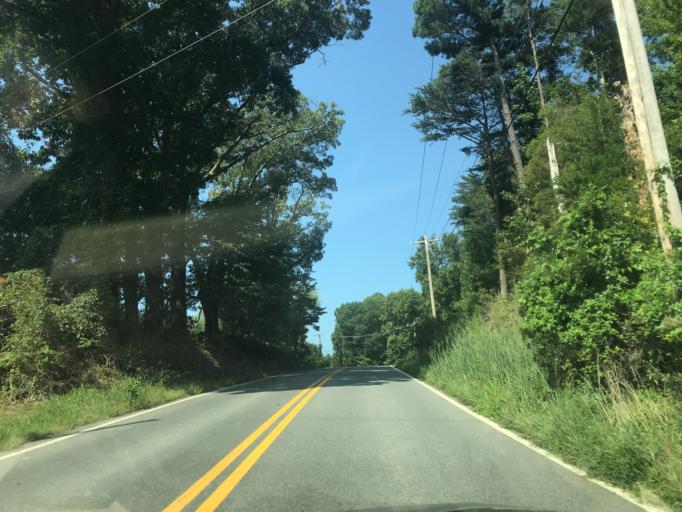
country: US
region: Maryland
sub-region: Calvert County
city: Prince Frederick
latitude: 38.4939
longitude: -76.6144
